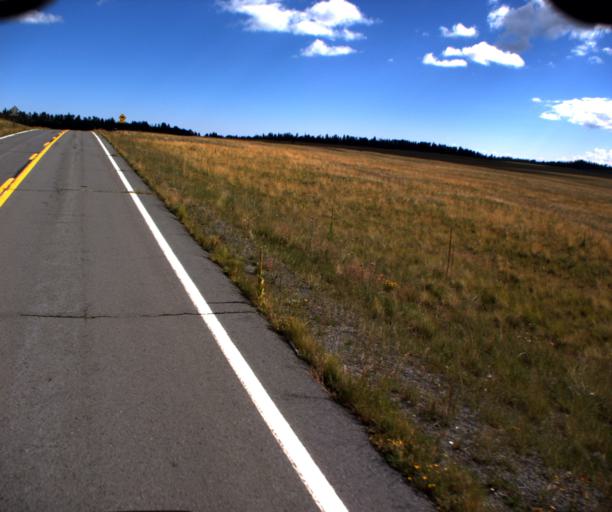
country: US
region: Arizona
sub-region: Apache County
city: Eagar
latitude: 33.9872
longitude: -109.3675
